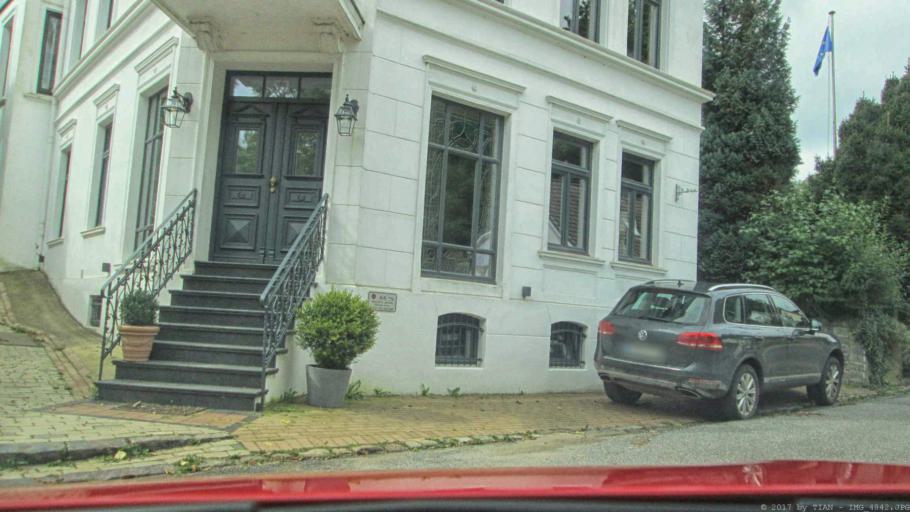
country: DE
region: Schleswig-Holstein
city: Halstenbek
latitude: 53.5604
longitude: 9.8032
